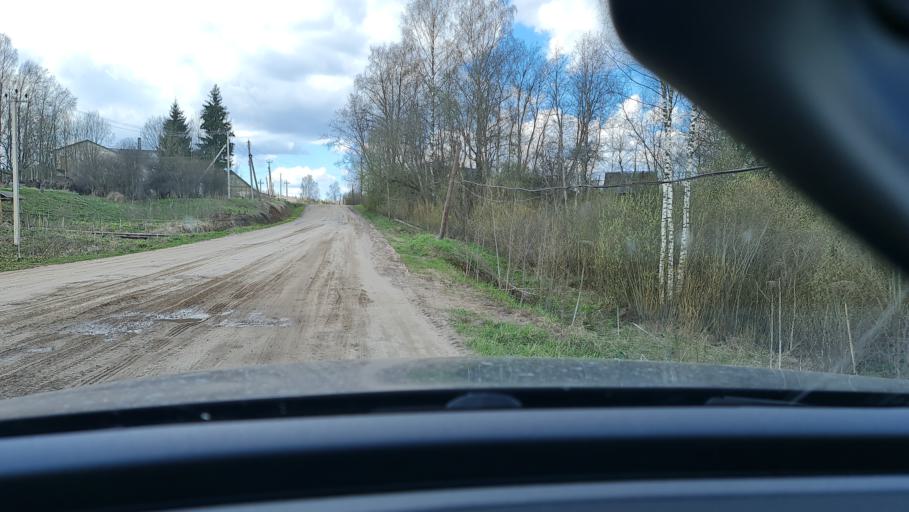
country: RU
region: Tverskaya
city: Toropets
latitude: 56.6442
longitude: 31.4241
